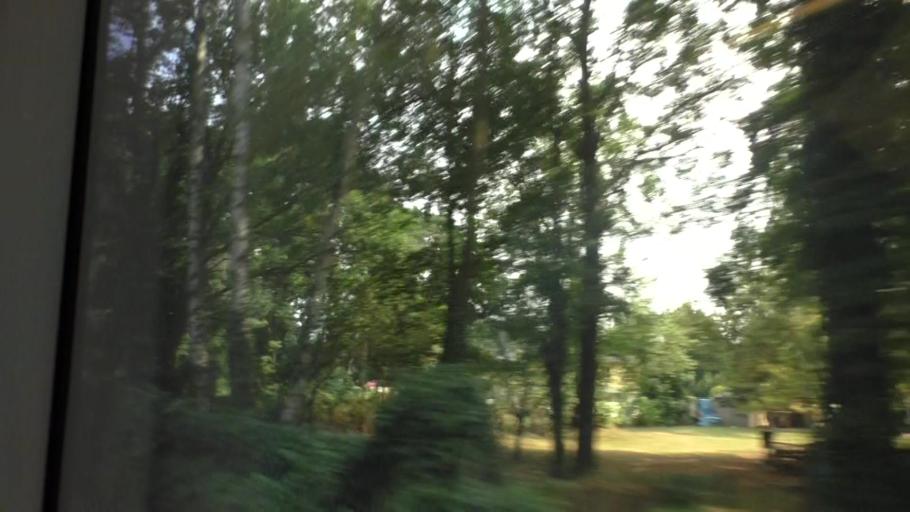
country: DE
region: Brandenburg
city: Konigs Wusterhausen
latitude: 52.2986
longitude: 13.6760
